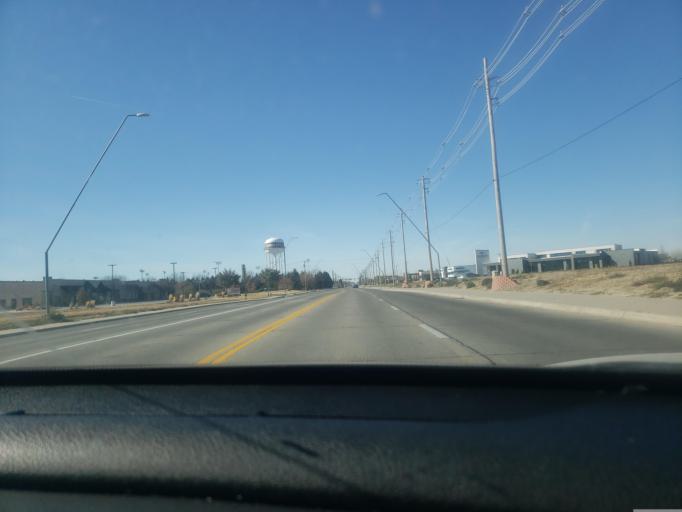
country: US
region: Kansas
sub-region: Finney County
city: Garden City
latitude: 37.9894
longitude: -100.8417
